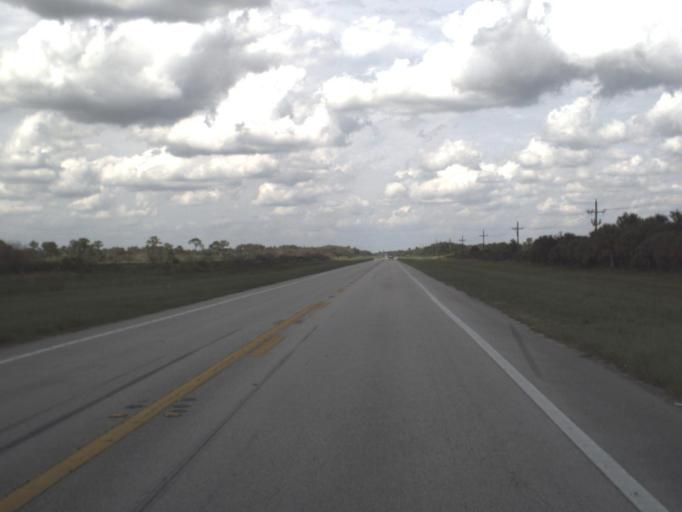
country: US
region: Florida
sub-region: Hendry County
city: Port LaBelle
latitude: 26.6409
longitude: -81.4363
